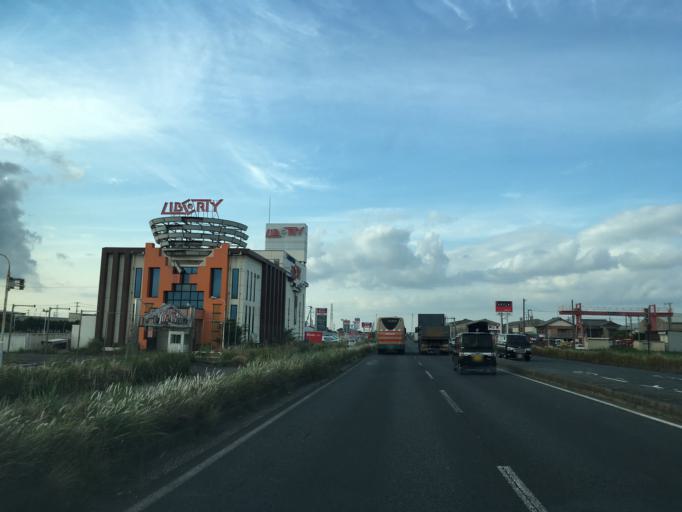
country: JP
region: Chiba
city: Kisarazu
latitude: 35.3960
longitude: 139.9412
